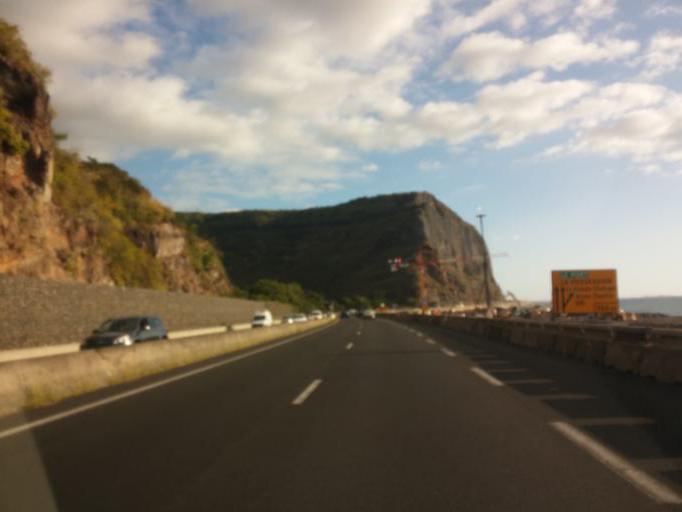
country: RE
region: Reunion
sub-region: Reunion
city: La Possession
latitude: -20.8935
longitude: 55.3789
